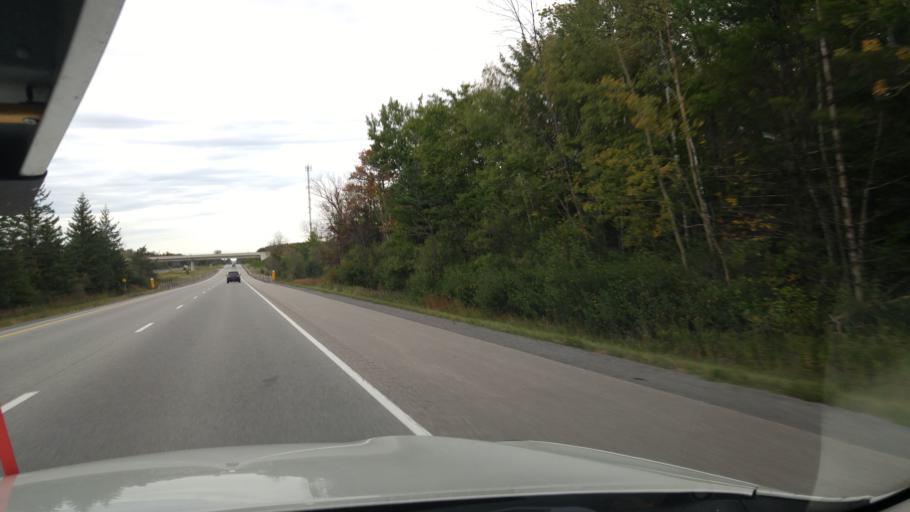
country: CA
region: Ontario
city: Carleton Place
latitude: 45.3205
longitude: -76.0956
